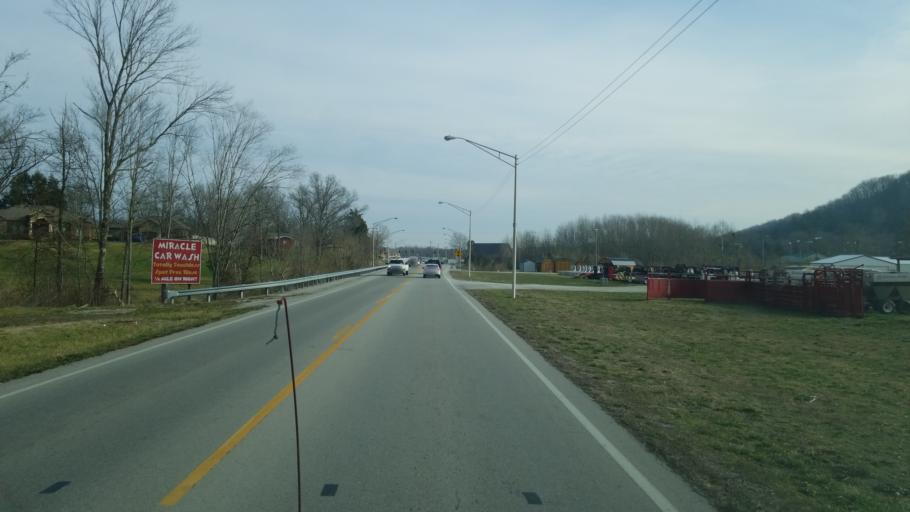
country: US
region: Kentucky
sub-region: Casey County
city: Liberty
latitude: 37.3128
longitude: -84.9359
